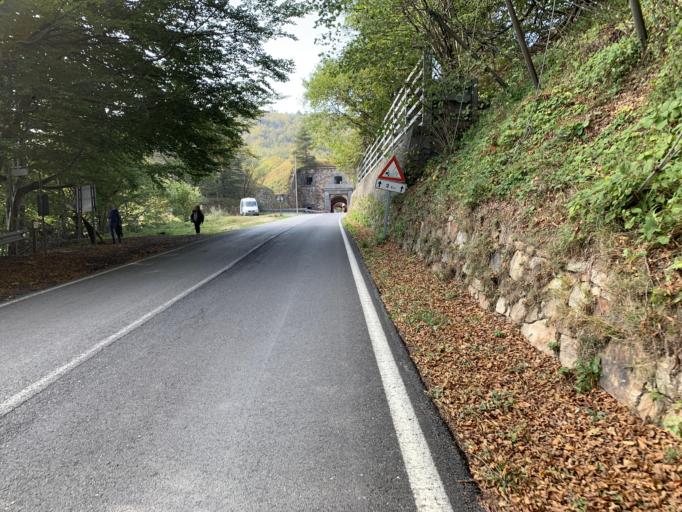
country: IT
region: Liguria
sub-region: Provincia di Savona
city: Osiglia
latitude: 44.2315
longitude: 8.1992
